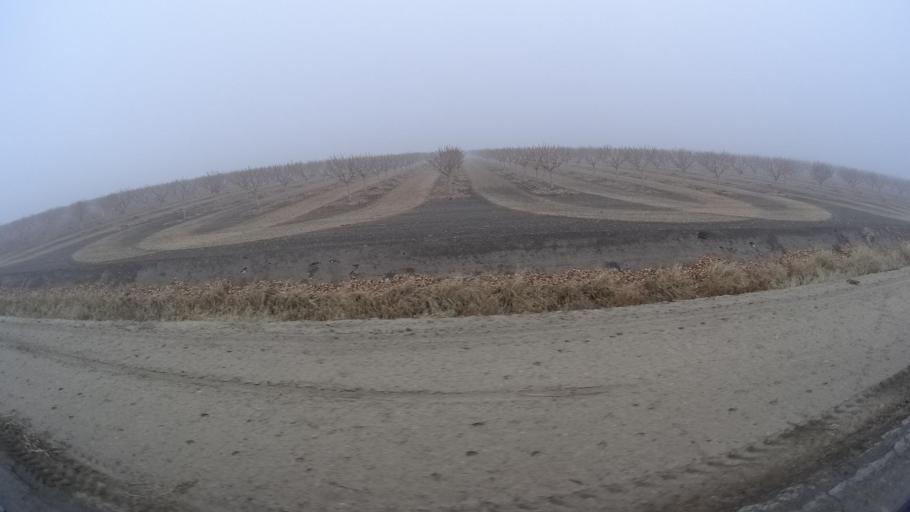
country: US
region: California
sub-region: Kern County
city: Buttonwillow
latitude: 35.4562
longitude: -119.5585
